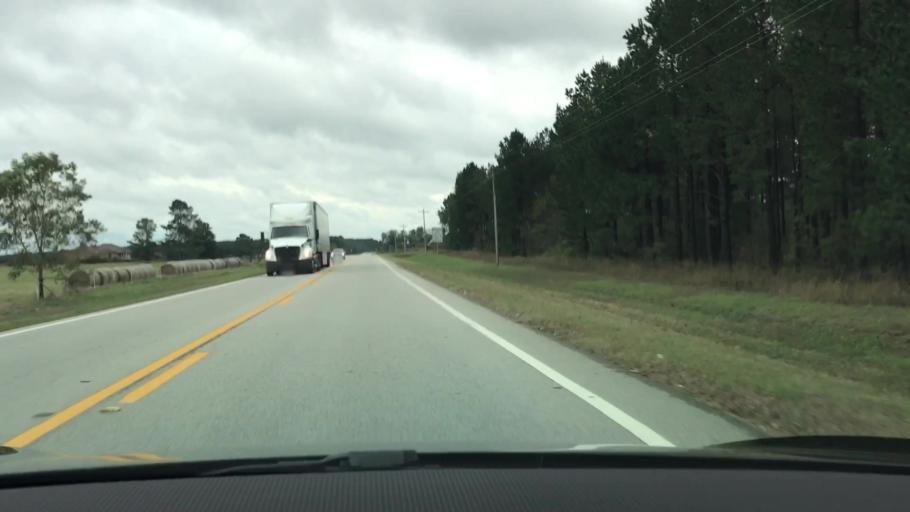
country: US
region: Georgia
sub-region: Glascock County
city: Gibson
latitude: 33.2946
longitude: -82.5124
